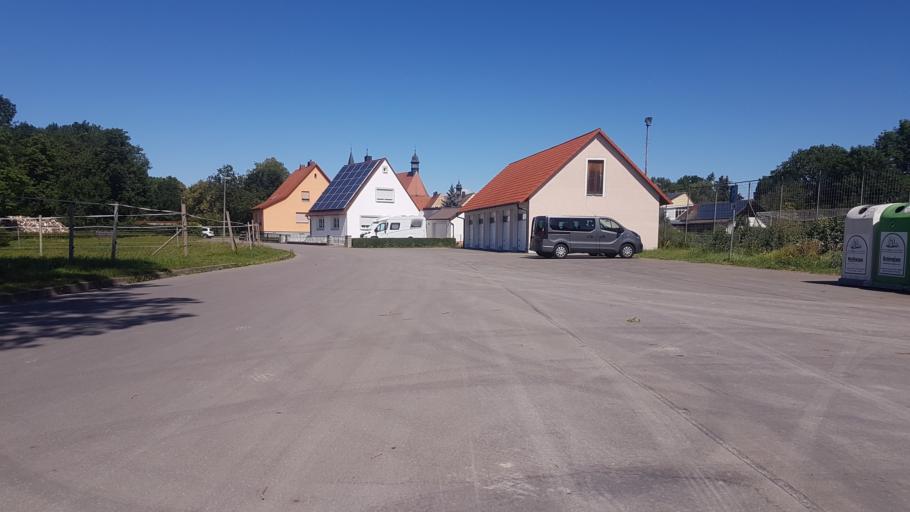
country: DE
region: Bavaria
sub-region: Regierungsbezirk Mittelfranken
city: Herrieden
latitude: 49.2300
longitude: 10.5009
